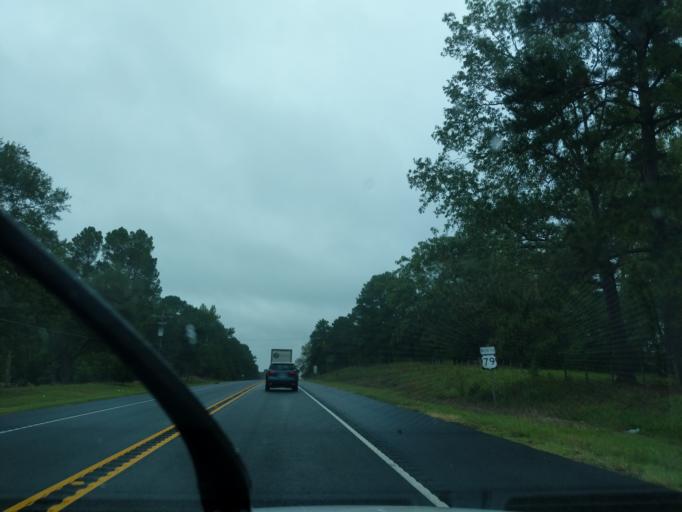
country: US
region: Louisiana
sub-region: Caddo Parish
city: Greenwood
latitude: 32.4288
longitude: -93.9847
